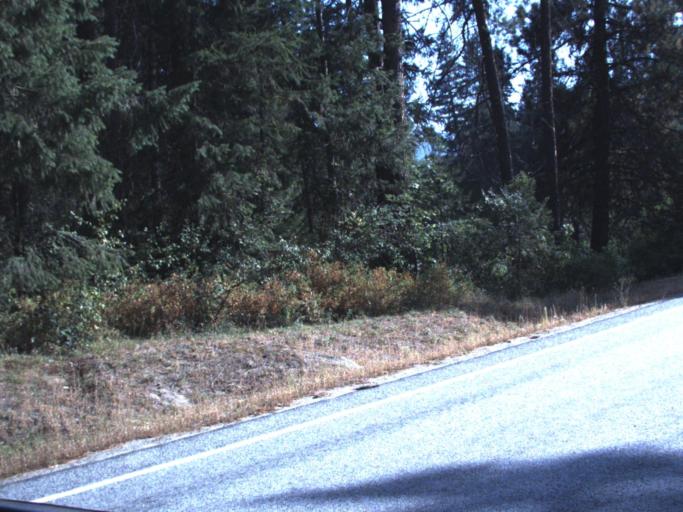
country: US
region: Washington
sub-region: Pend Oreille County
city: Newport
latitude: 48.1169
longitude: -117.2741
